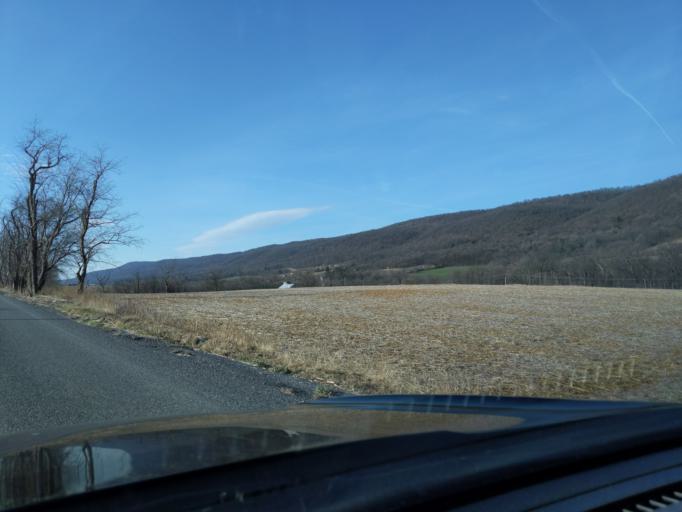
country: US
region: Pennsylvania
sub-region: Blair County
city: Williamsburg
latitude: 40.4156
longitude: -78.2717
